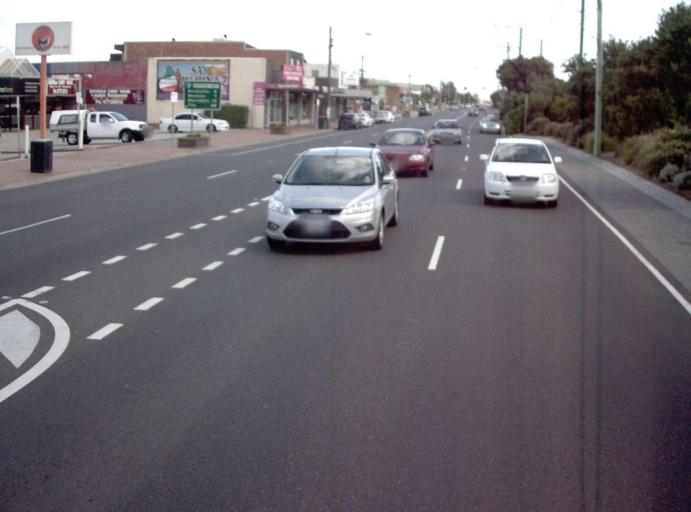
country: AU
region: Victoria
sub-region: Kingston
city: Edithvale
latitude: -38.0365
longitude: 145.1074
